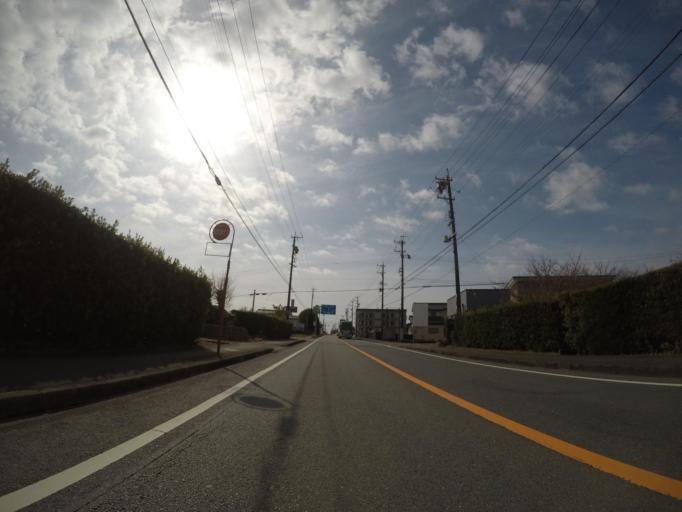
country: JP
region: Shizuoka
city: Hamakita
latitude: 34.8014
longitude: 137.6974
